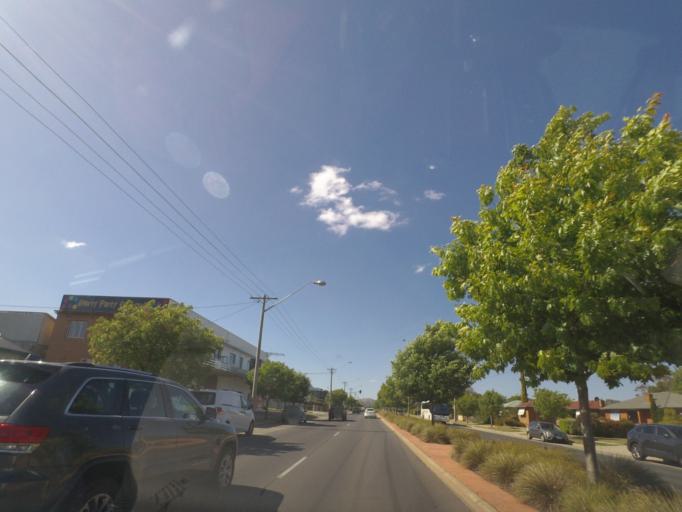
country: AU
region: New South Wales
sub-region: Albury Municipality
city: North Albury
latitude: -36.0617
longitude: 146.9318
